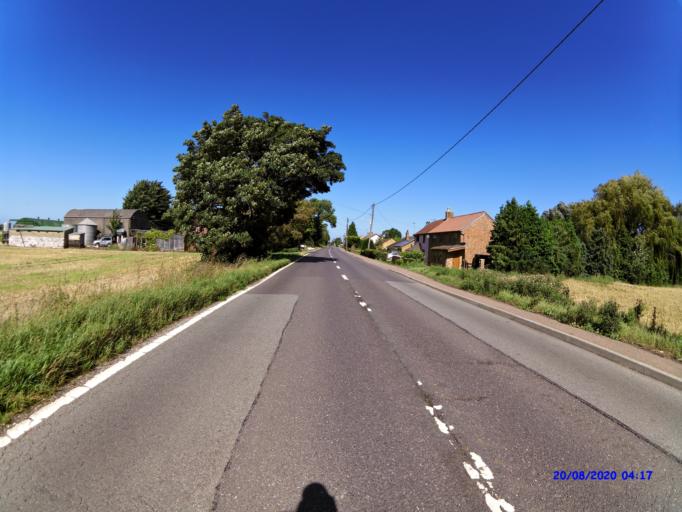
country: GB
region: England
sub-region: Cambridgeshire
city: Ramsey
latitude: 52.4898
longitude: -0.1153
